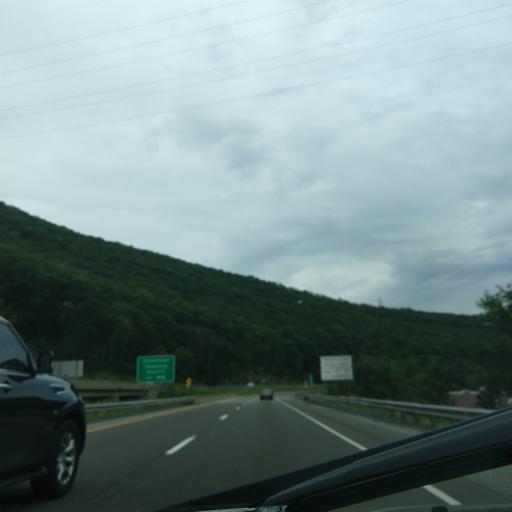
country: US
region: Pennsylvania
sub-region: Lackawanna County
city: Chinchilla
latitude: 41.4693
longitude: -75.6713
